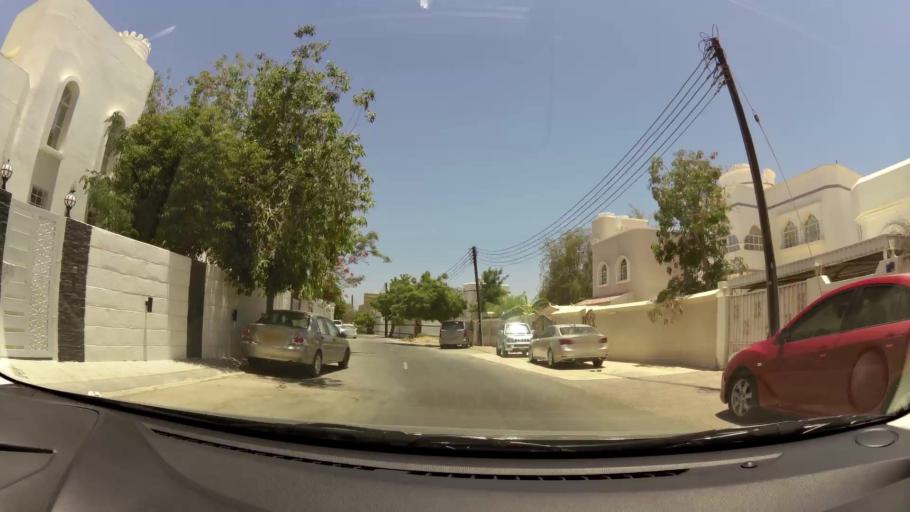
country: OM
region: Muhafazat Masqat
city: As Sib al Jadidah
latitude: 23.6307
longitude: 58.2402
